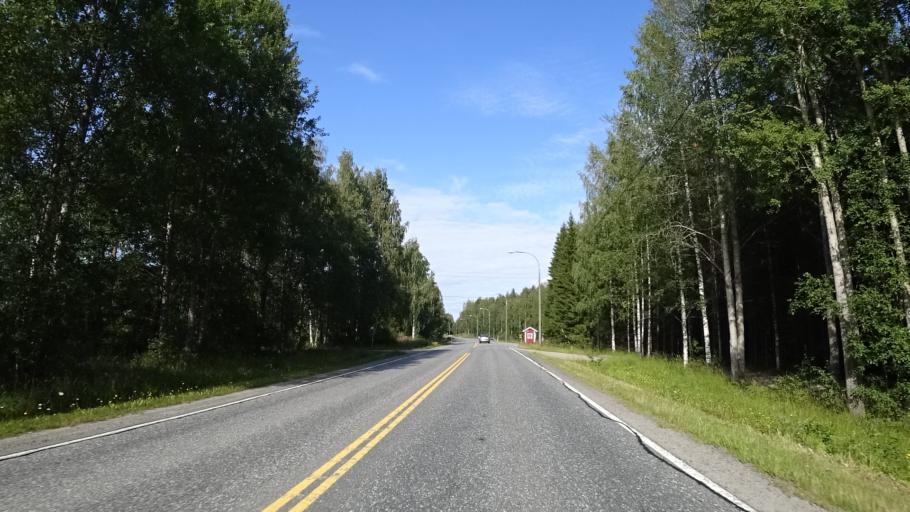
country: FI
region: North Karelia
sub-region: Joensuu
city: Eno
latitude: 62.7837
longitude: 30.0768
